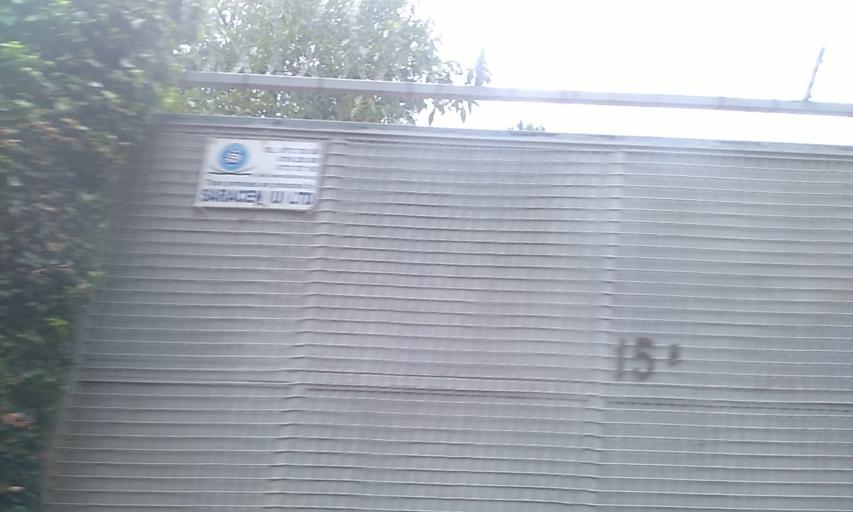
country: UG
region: Central Region
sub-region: Kampala District
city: Kampala
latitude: 0.3309
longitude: 32.5934
